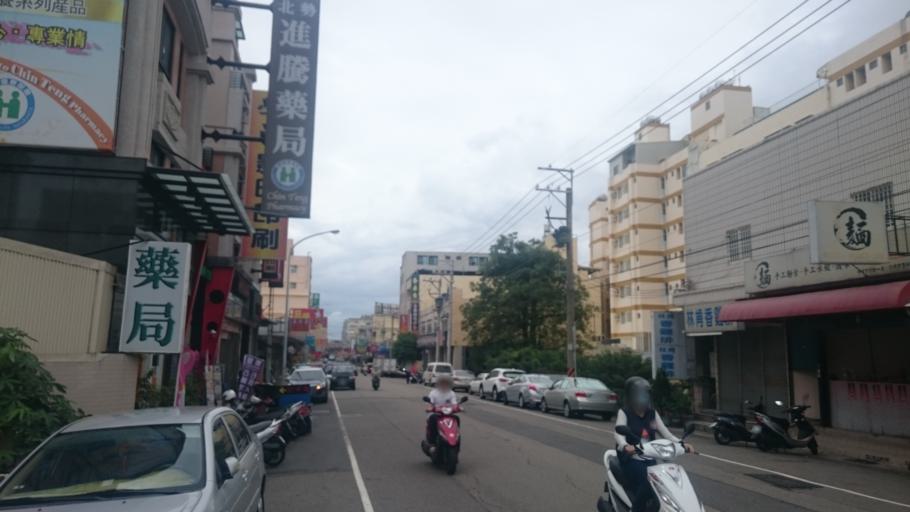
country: TW
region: Taiwan
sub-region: Taichung City
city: Taichung
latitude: 24.2252
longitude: 120.5762
